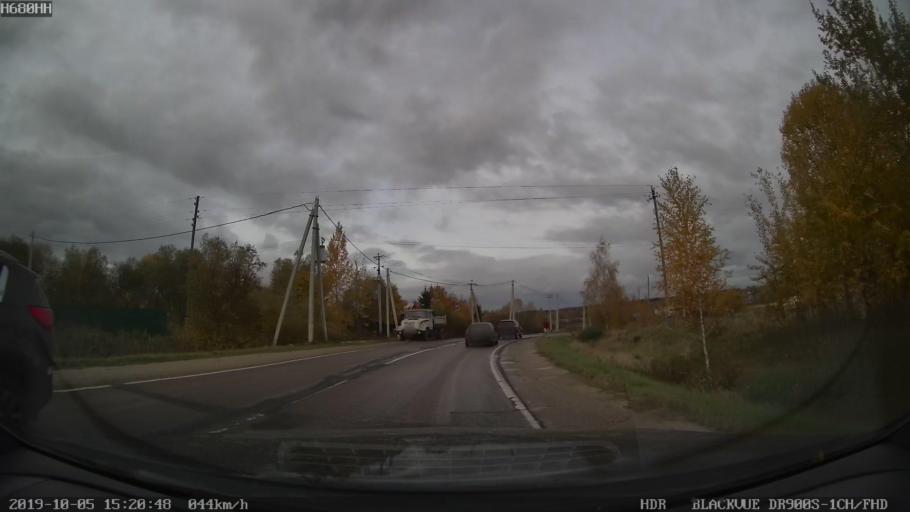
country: RU
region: Moskovskaya
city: Solnechnogorsk
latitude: 56.2252
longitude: 36.9076
